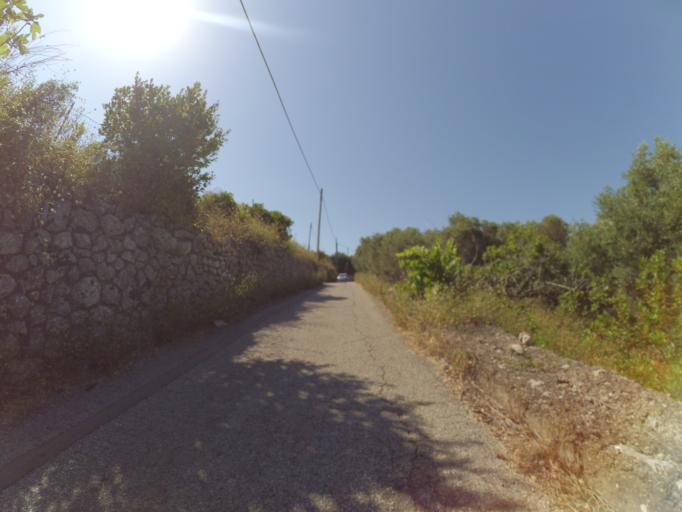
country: IT
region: Latium
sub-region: Provincia di Latina
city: Gaeta
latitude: 41.2202
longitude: 13.5488
